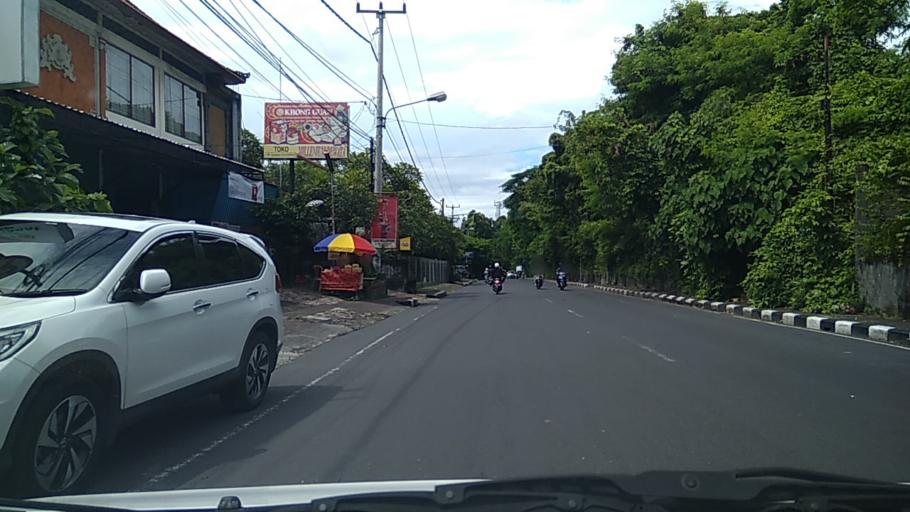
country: ID
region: Bali
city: Dajan Tangluk
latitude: -8.6437
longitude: 115.2489
